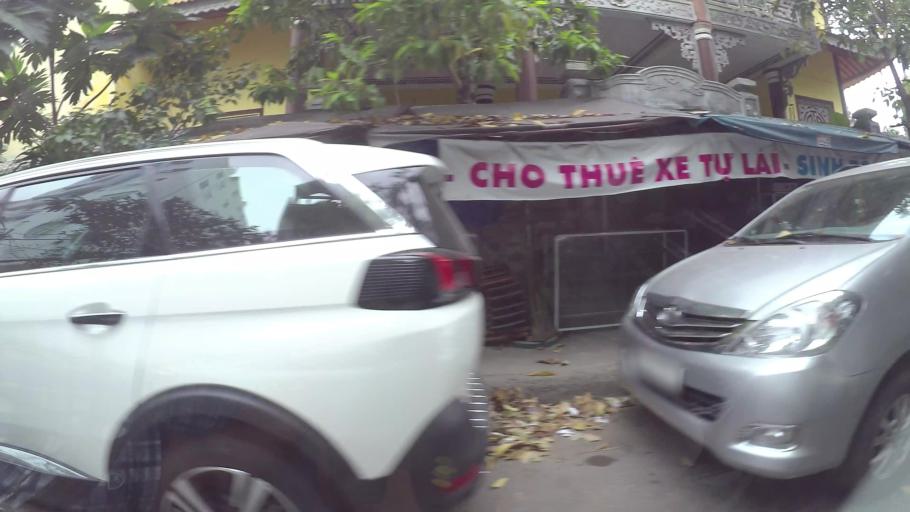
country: VN
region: Da Nang
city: Da Nang
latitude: 16.0589
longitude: 108.2098
